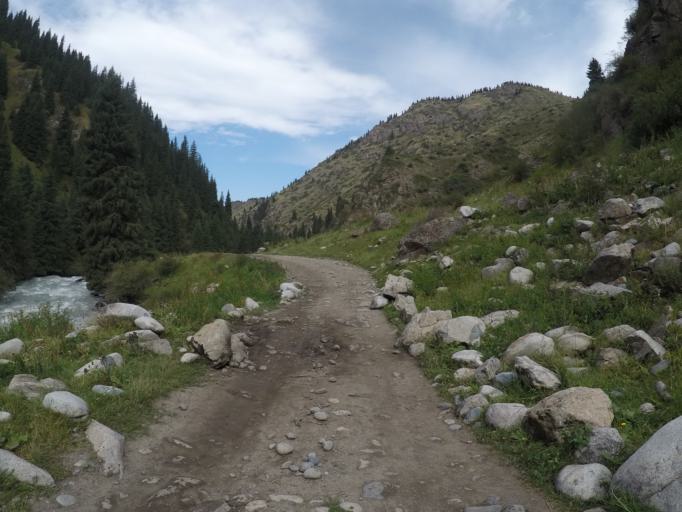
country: KG
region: Ysyk-Koel
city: Teploklyuchenka
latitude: 42.4387
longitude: 78.5589
